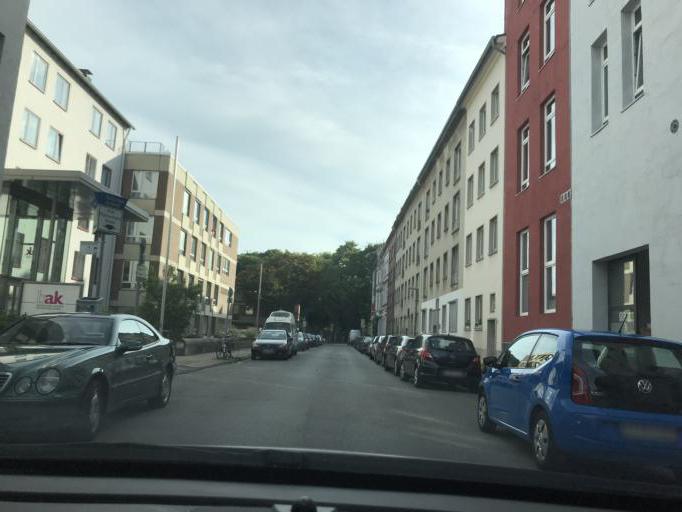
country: DE
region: North Rhine-Westphalia
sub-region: Regierungsbezirk Koln
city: Aachen
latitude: 50.7670
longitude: 6.0847
